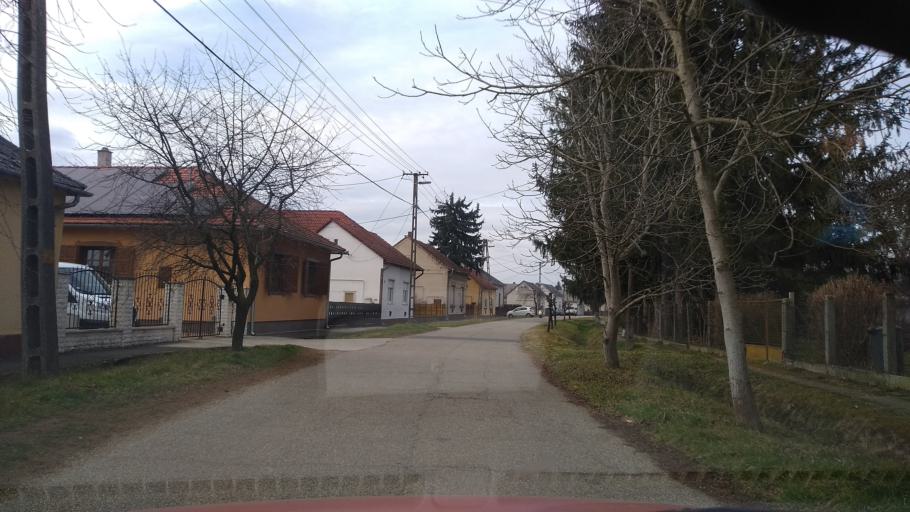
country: HU
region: Somogy
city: Barcs
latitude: 45.9592
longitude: 17.4490
